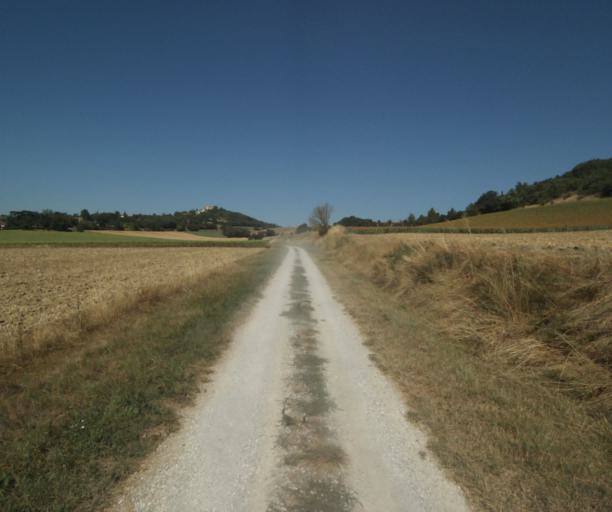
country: FR
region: Midi-Pyrenees
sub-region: Departement de la Haute-Garonne
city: Revel
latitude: 43.5094
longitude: 1.9479
